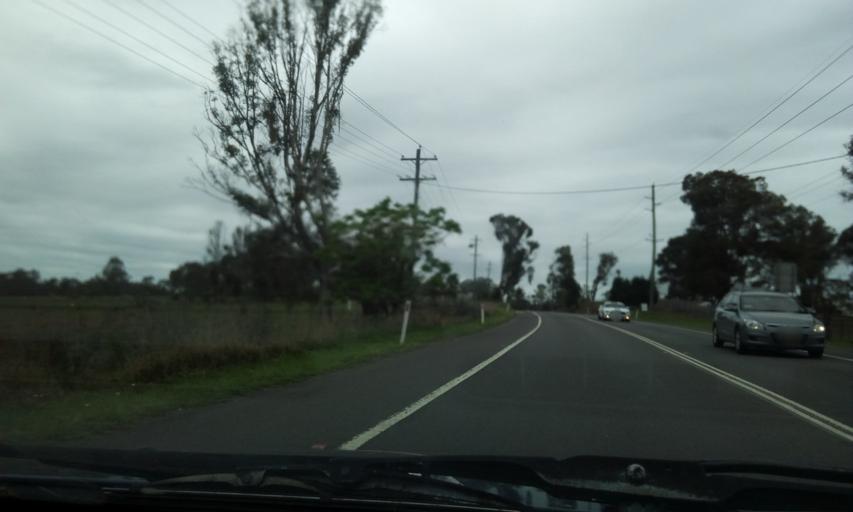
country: AU
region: New South Wales
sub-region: Penrith Municipality
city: Mulgoa
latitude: -33.8340
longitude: 150.6828
